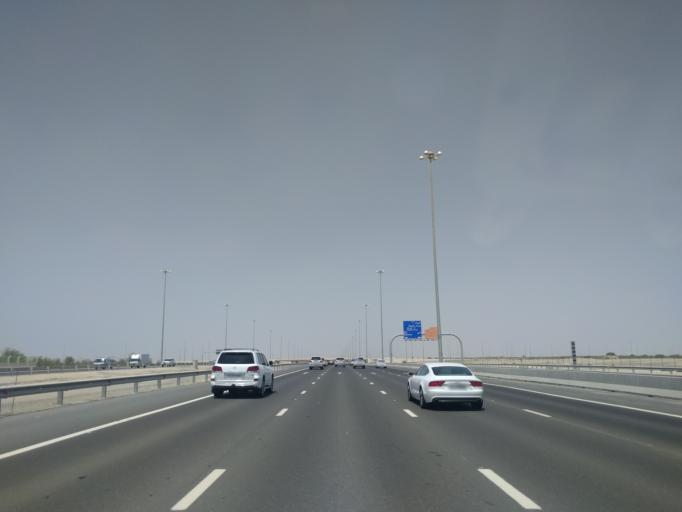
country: AE
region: Abu Dhabi
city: Abu Dhabi
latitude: 24.6881
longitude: 54.7748
